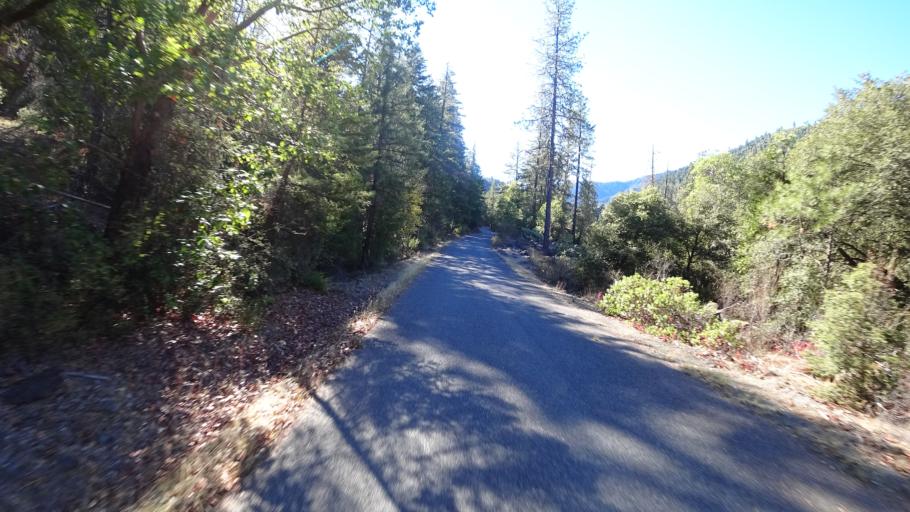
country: US
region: California
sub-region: Humboldt County
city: Willow Creek
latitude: 41.1922
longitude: -123.2158
